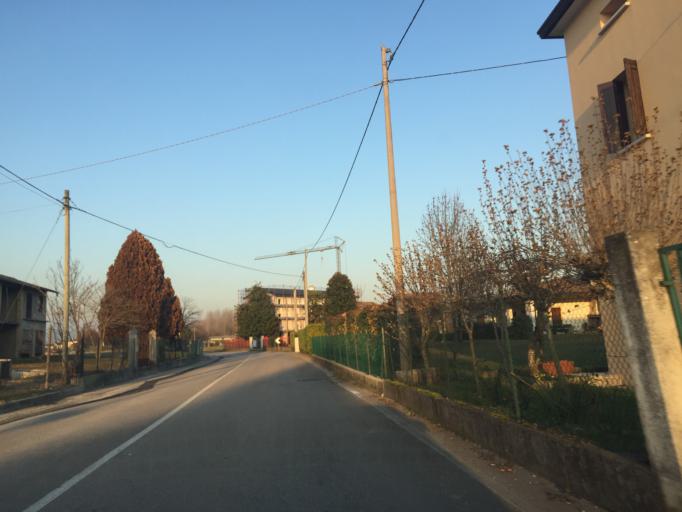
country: IT
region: Friuli Venezia Giulia
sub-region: Provincia di Pordenone
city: Sacile
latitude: 45.9676
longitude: 12.5236
